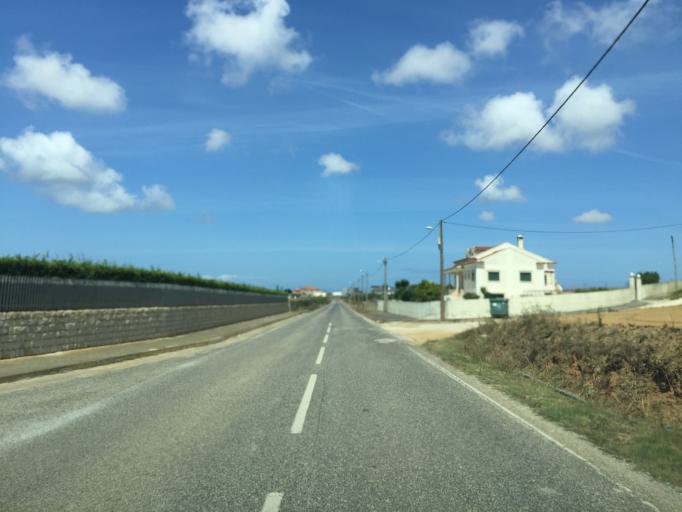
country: PT
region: Leiria
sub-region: Peniche
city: Atouguia da Baleia
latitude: 39.2888
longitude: -9.3063
